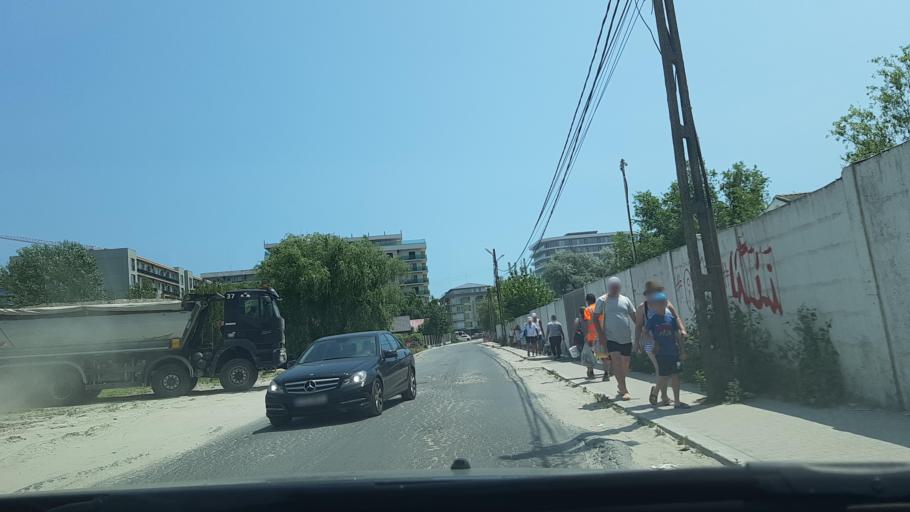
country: RO
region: Constanta
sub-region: Comuna Navodari
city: Navodari
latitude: 44.2891
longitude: 28.6187
